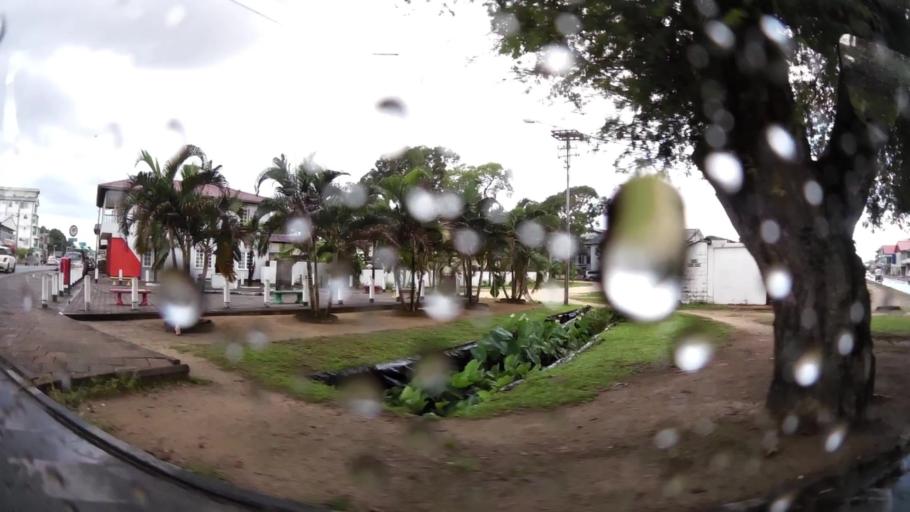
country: SR
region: Paramaribo
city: Paramaribo
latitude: 5.8341
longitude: -55.1656
